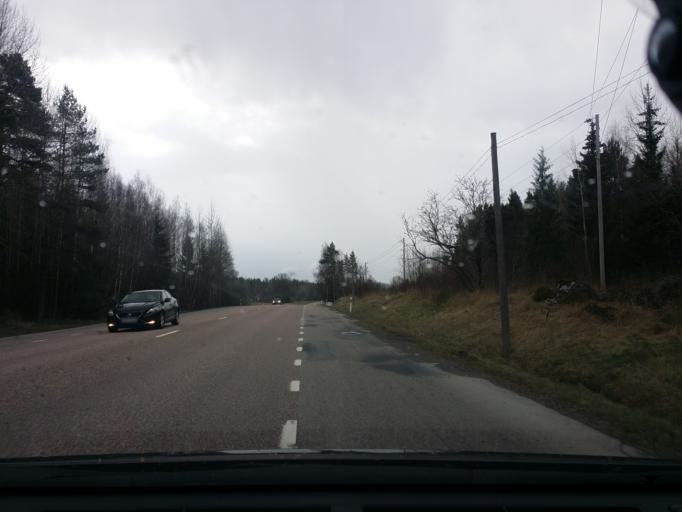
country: SE
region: Uppsala
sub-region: Enkopings Kommun
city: Irsta
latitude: 59.7170
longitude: 16.9701
